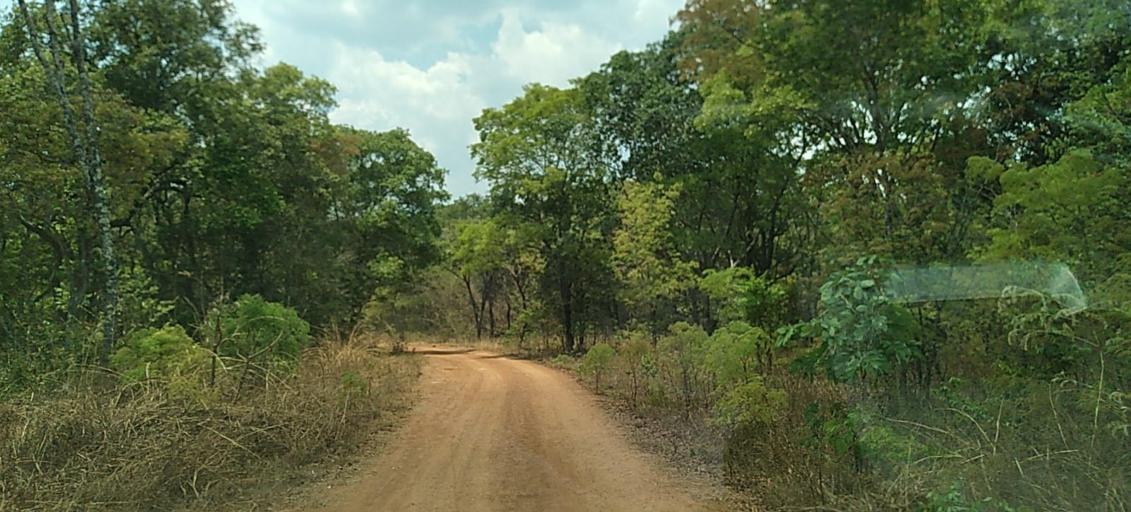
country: ZM
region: Copperbelt
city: Chingola
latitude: -12.8021
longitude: 27.6428
